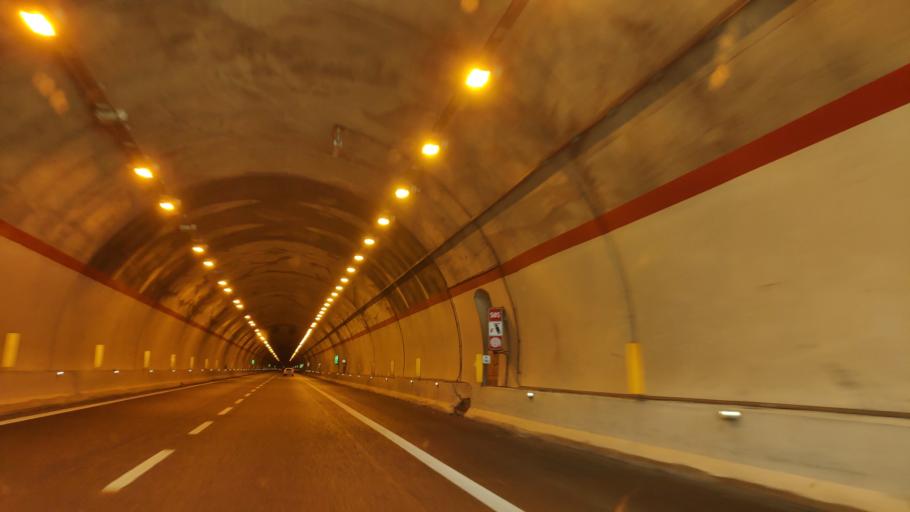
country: IT
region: Calabria
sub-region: Provincia di Cosenza
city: Morano Calabro
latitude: 39.8767
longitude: 16.1266
